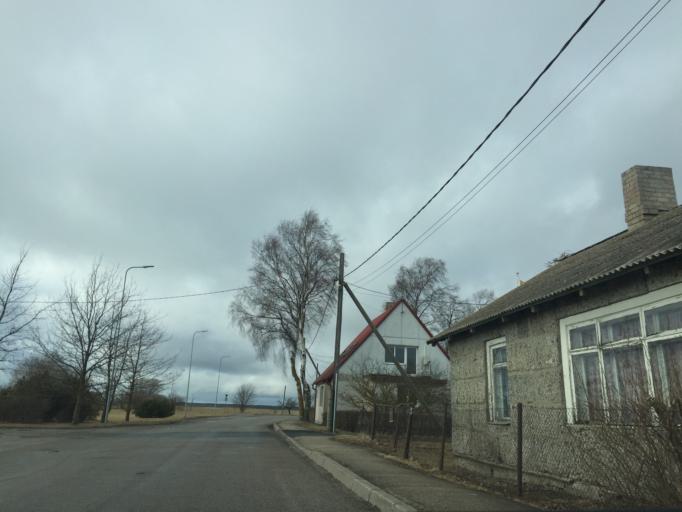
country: EE
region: Laeaene
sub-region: Haapsalu linn
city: Haapsalu
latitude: 58.9536
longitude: 23.5232
